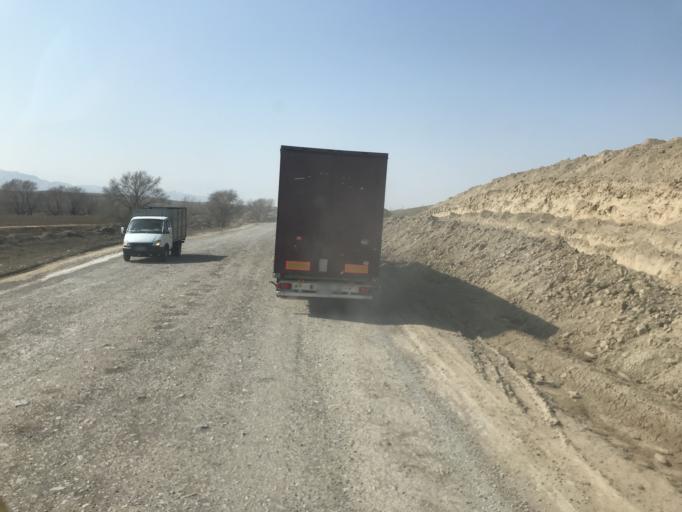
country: KG
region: Chuy
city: Bystrovka
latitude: 43.3224
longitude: 75.8060
